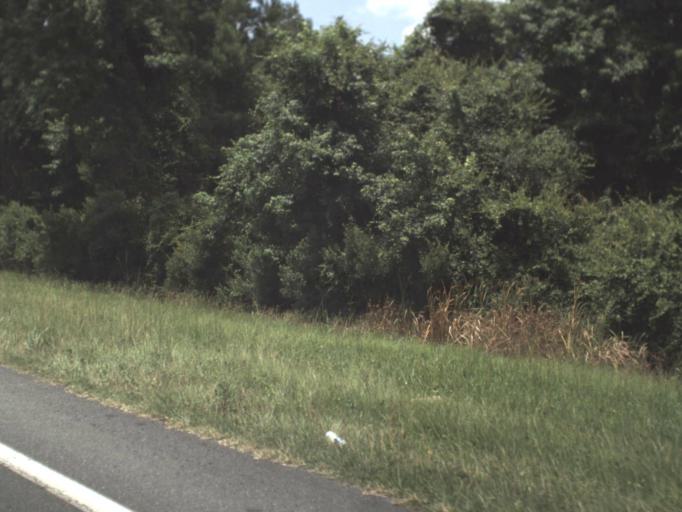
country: US
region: Florida
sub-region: Columbia County
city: Five Points
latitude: 30.2058
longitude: -82.6462
